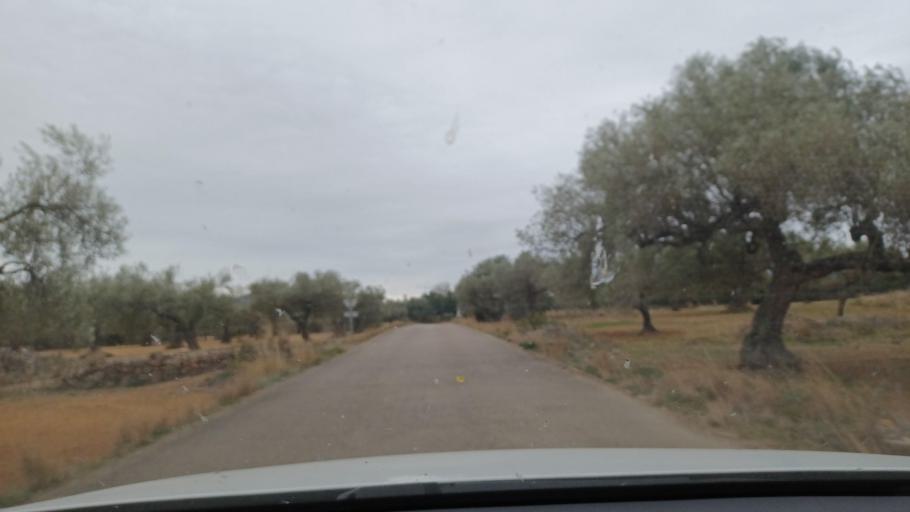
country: ES
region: Valencia
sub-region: Provincia de Castello
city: Canet lo Roig
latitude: 40.5815
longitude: 0.2825
